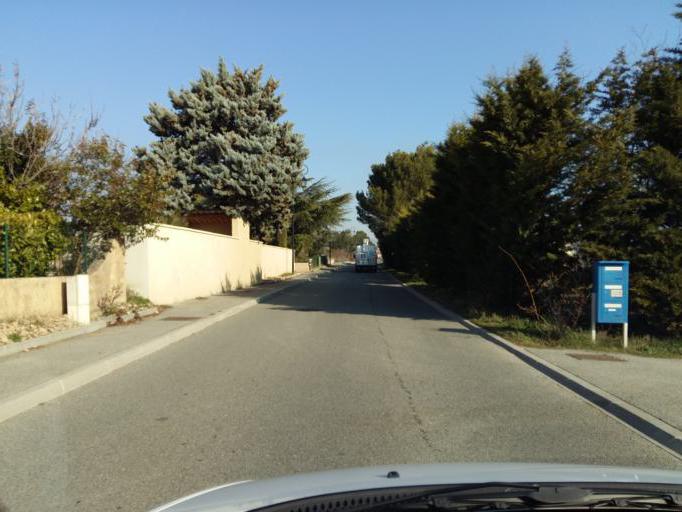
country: FR
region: Provence-Alpes-Cote d'Azur
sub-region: Departement du Vaucluse
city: Vaison-la-Romaine
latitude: 44.2479
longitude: 5.0179
